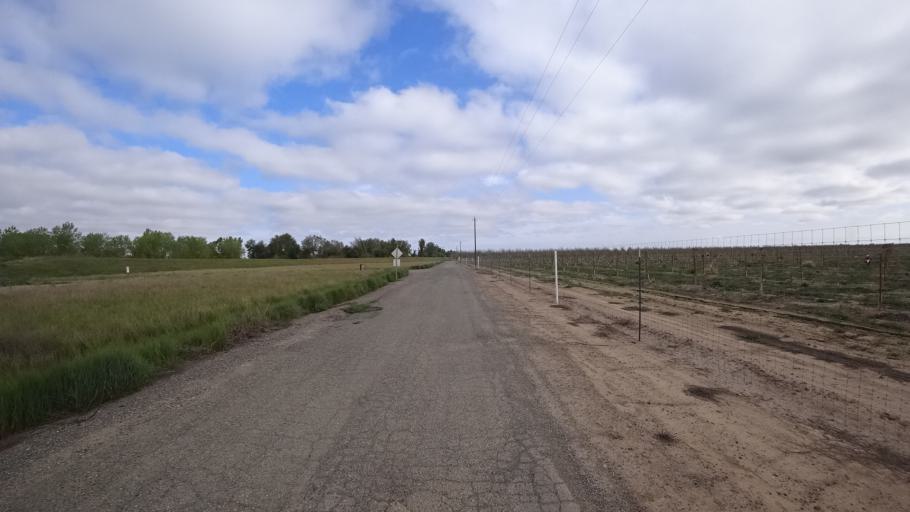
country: US
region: California
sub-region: Colusa County
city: Colusa
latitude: 39.4156
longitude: -121.9922
